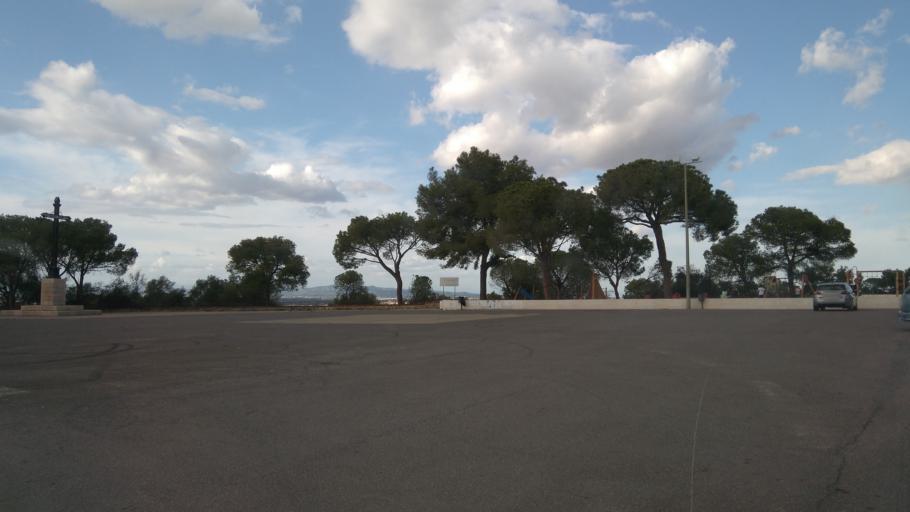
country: ES
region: Valencia
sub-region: Provincia de Valencia
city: Alzira
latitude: 39.1524
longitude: -0.4194
